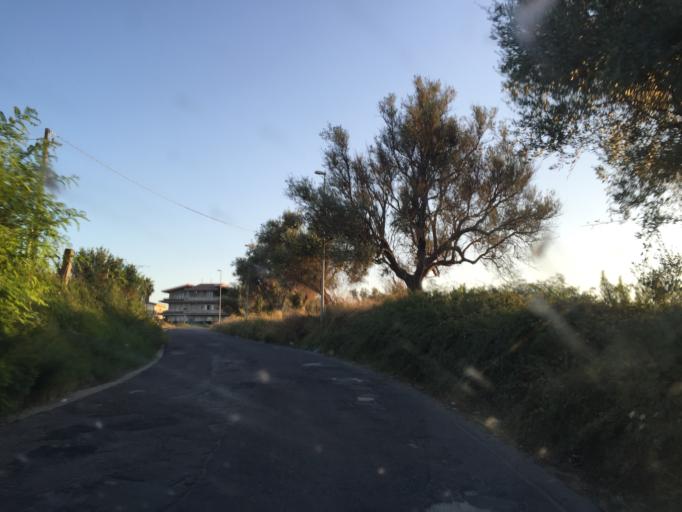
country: IT
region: Calabria
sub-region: Provincia di Vibo-Valentia
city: Pannaconi
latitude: 38.7043
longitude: 16.0483
